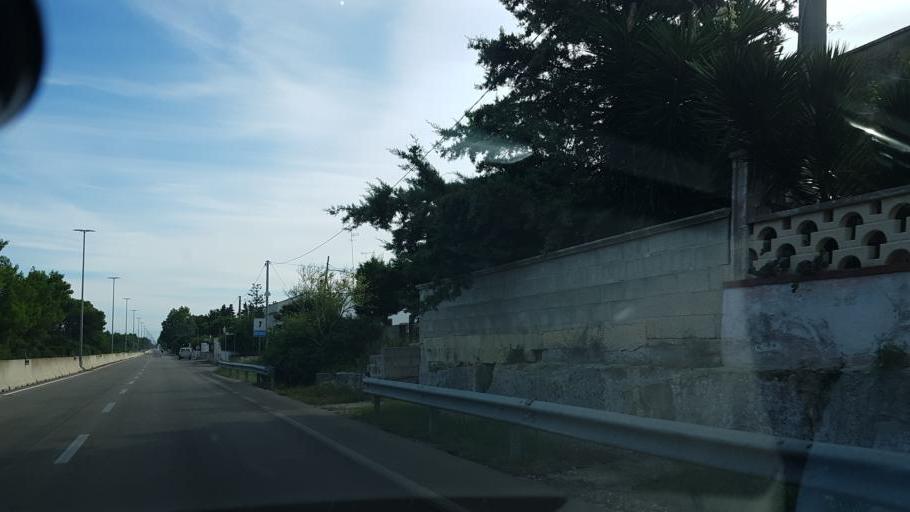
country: IT
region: Apulia
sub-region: Provincia di Lecce
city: Struda
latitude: 40.3840
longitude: 18.2834
